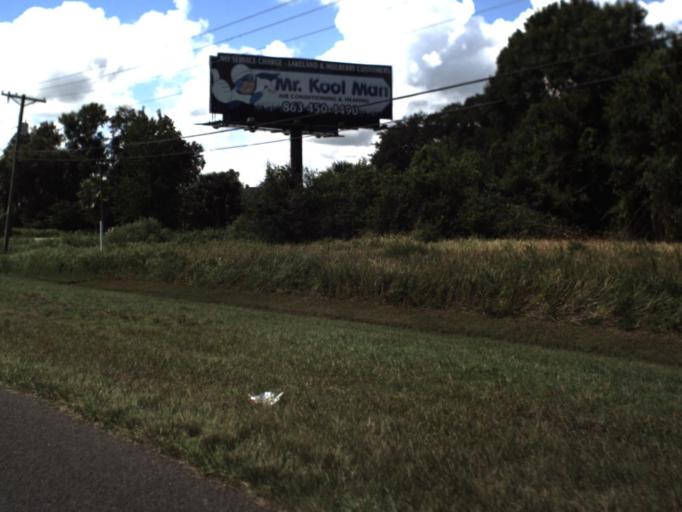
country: US
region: Florida
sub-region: Polk County
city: Medulla
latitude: 27.9355
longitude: -81.9742
